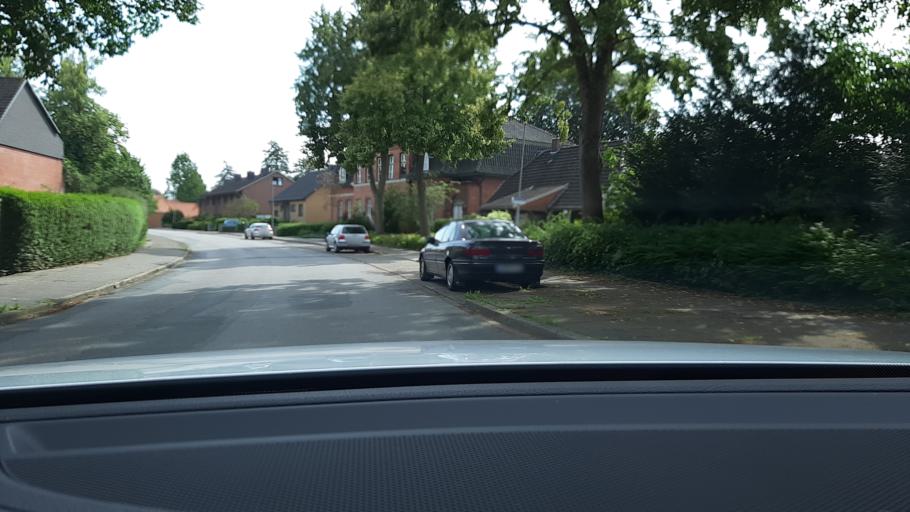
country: DE
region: Schleswig-Holstein
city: Reinfeld
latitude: 53.8340
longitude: 10.4785
